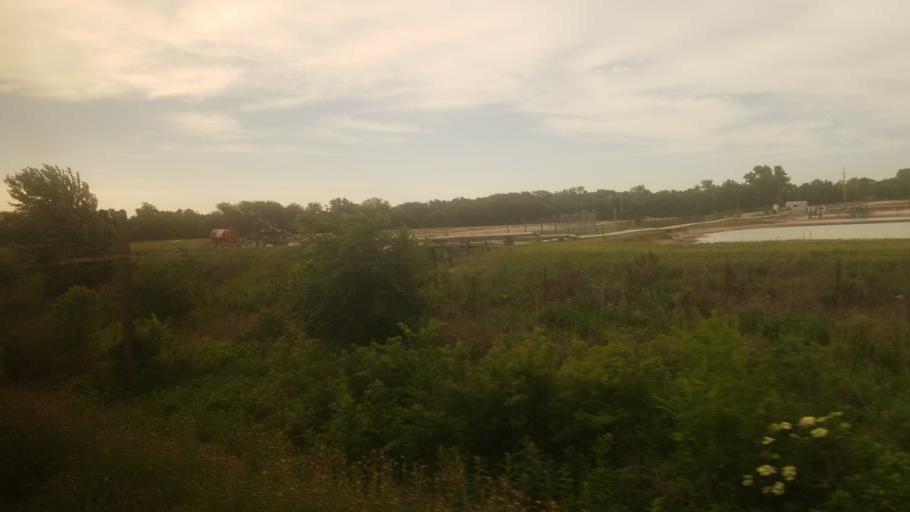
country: US
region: Kansas
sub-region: Shawnee County
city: Topeka
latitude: 39.0590
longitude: -95.5571
